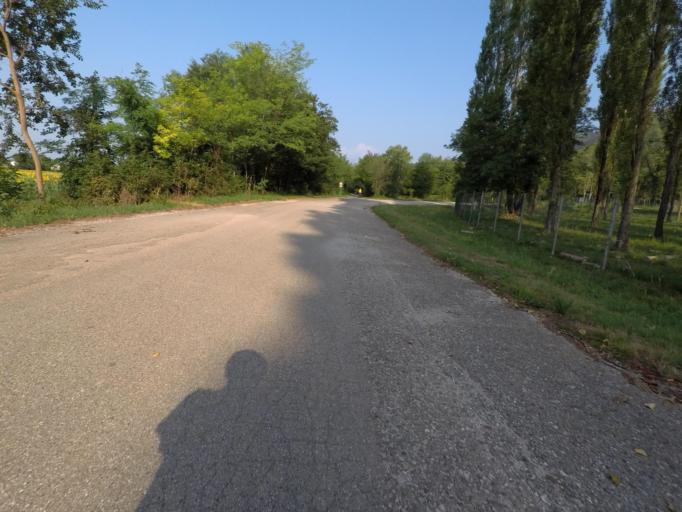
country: IT
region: Friuli Venezia Giulia
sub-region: Provincia di Pordenone
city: Travesio
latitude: 46.2015
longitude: 12.8414
